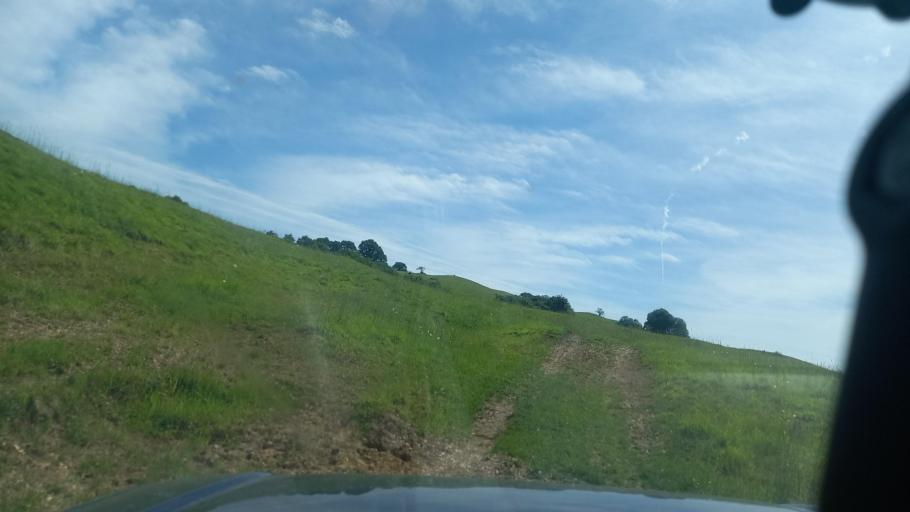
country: RU
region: Karachayevo-Cherkesiya
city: Kurdzhinovo
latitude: 44.1444
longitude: 41.0627
